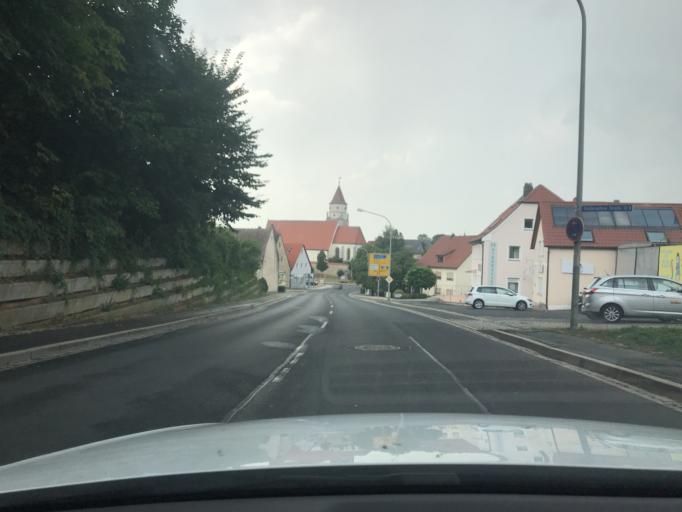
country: DE
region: Bavaria
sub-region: Upper Palatinate
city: Speinshart
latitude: 49.7518
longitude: 11.8356
